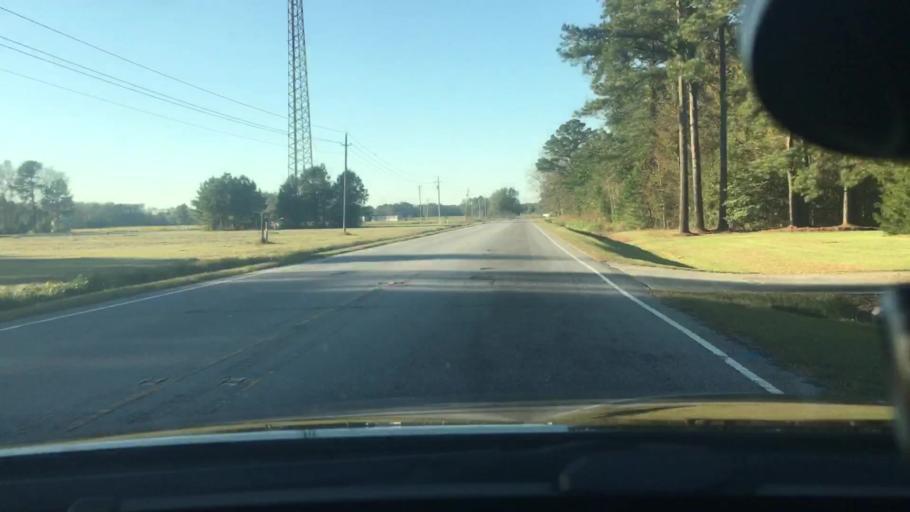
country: US
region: North Carolina
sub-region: Craven County
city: Vanceboro
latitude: 35.4204
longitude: -77.2580
